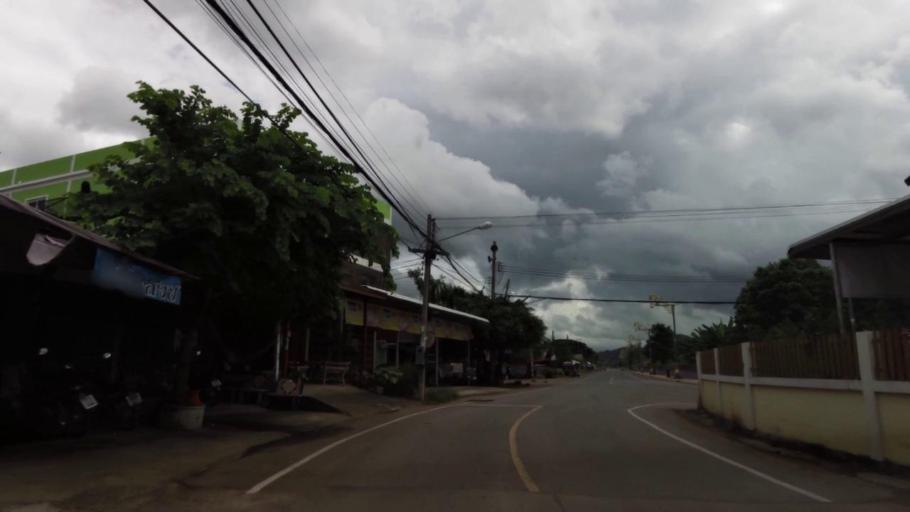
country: TH
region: Nakhon Sawan
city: Phai Sali
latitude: 15.5997
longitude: 100.6539
